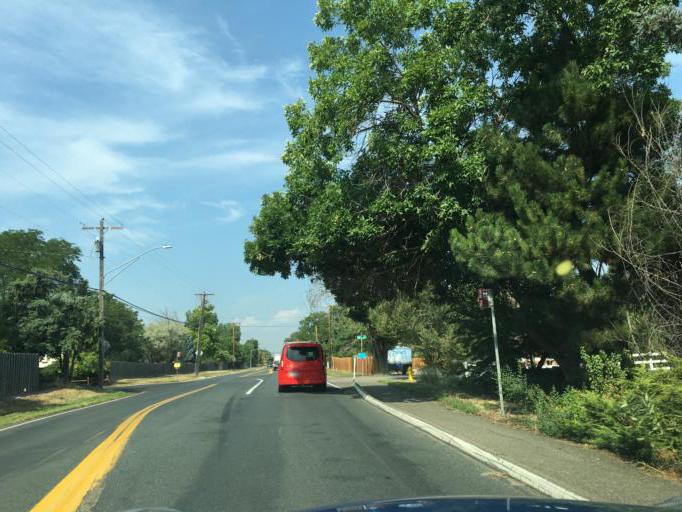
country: US
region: Colorado
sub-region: Jefferson County
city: Arvada
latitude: 39.8420
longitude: -105.1188
